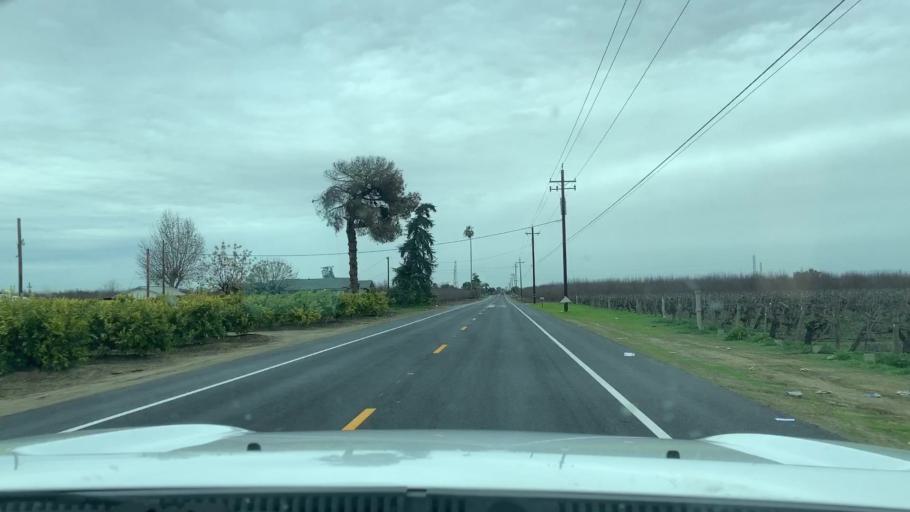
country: US
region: California
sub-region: Fresno County
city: Fowler
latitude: 36.5861
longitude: -119.6825
